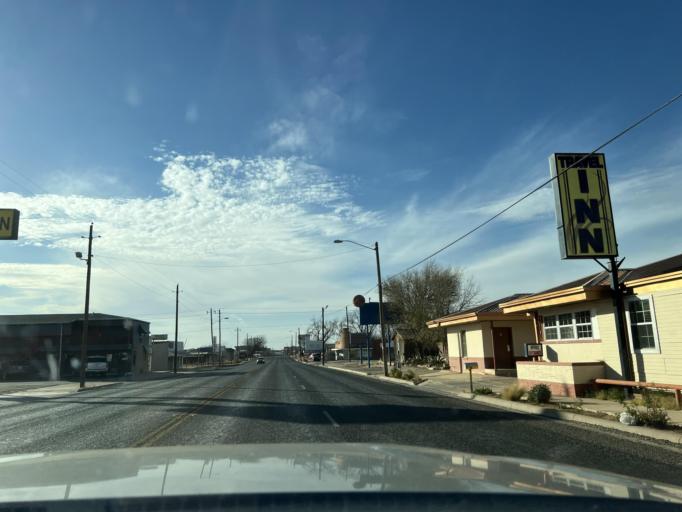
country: US
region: Texas
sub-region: Scurry County
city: Snyder
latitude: 32.7170
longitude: -100.9078
